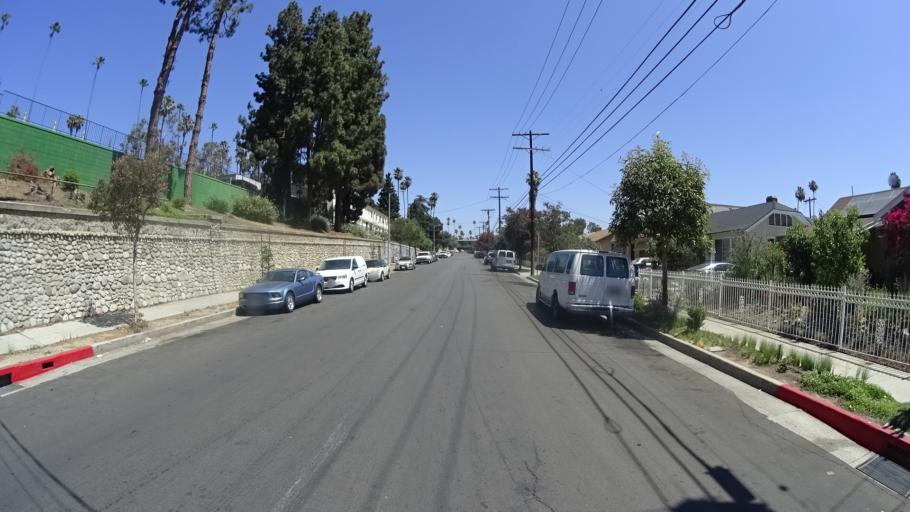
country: US
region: California
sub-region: Los Angeles County
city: View Park-Windsor Hills
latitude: 34.0346
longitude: -118.3058
